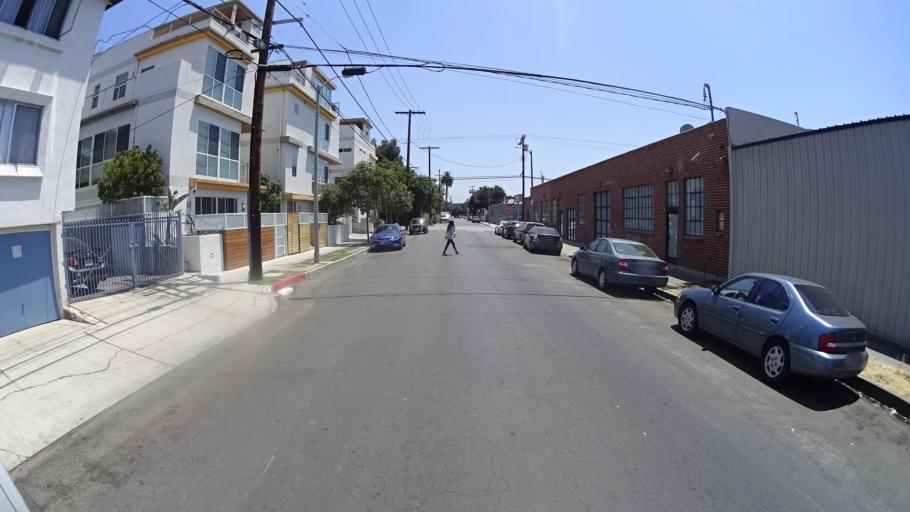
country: US
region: California
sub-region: Los Angeles County
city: Hollywood
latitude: 34.0926
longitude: -118.3370
